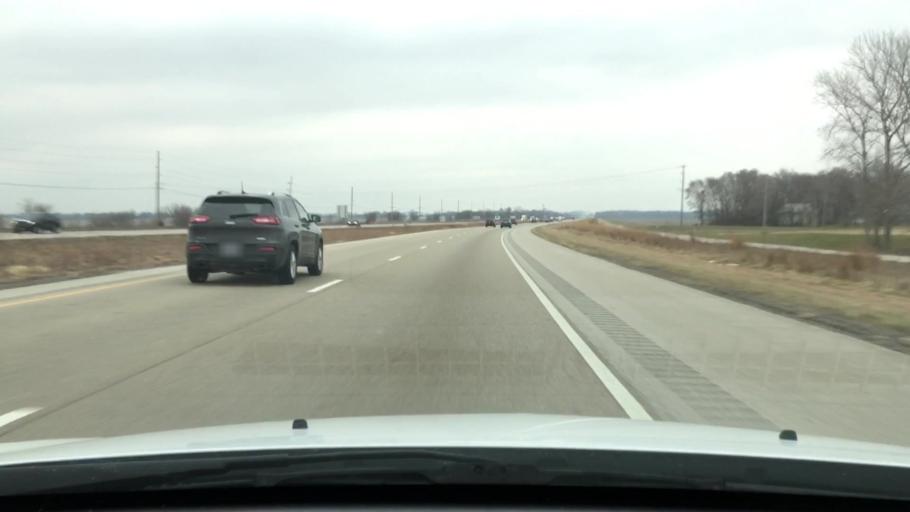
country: US
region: Illinois
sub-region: Logan County
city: Lincoln
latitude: 40.1996
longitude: -89.3018
